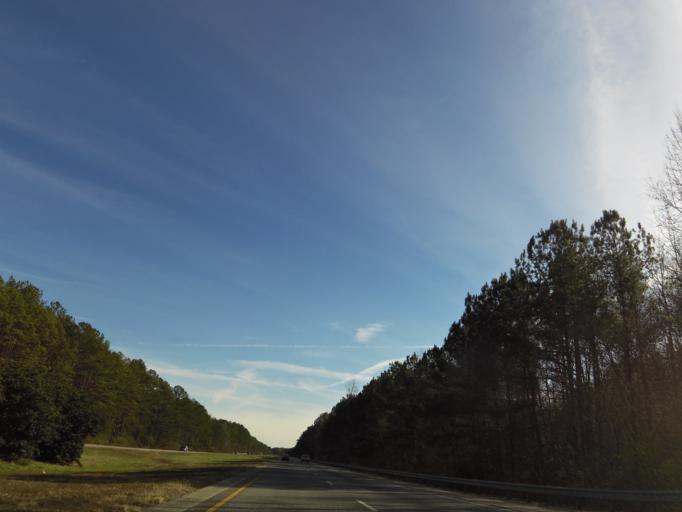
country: US
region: Georgia
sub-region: Harris County
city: Hamilton
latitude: 32.7170
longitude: -85.0177
